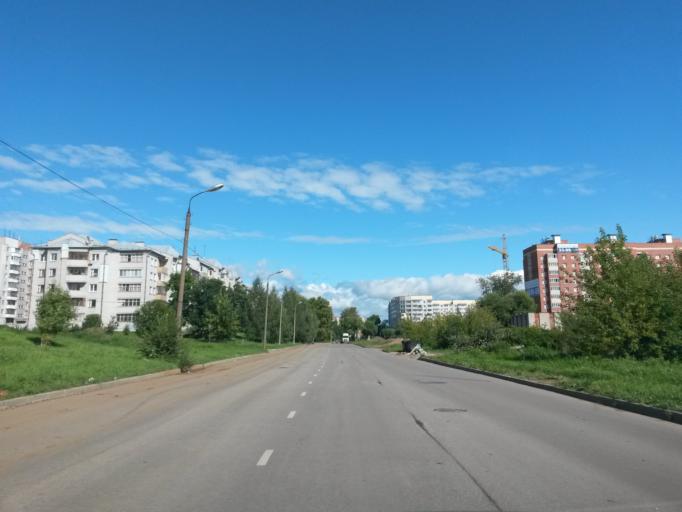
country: RU
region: Jaroslavl
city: Yaroslavl
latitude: 57.5848
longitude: 39.8657
